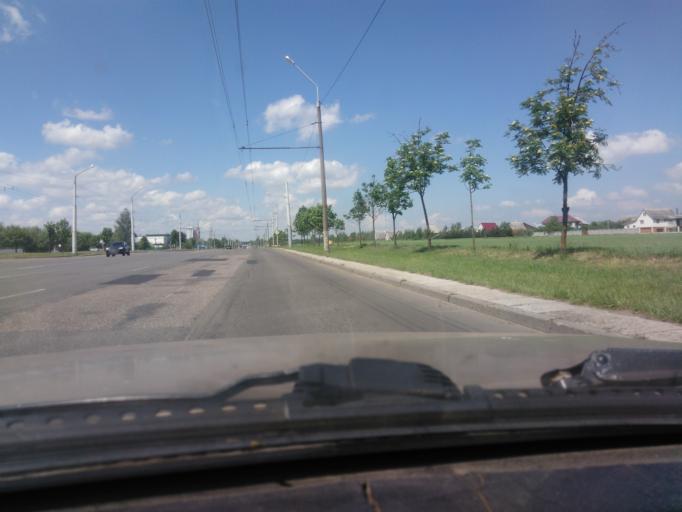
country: BY
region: Mogilev
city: Palykavichy Pyershyya
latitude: 53.9620
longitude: 30.3580
